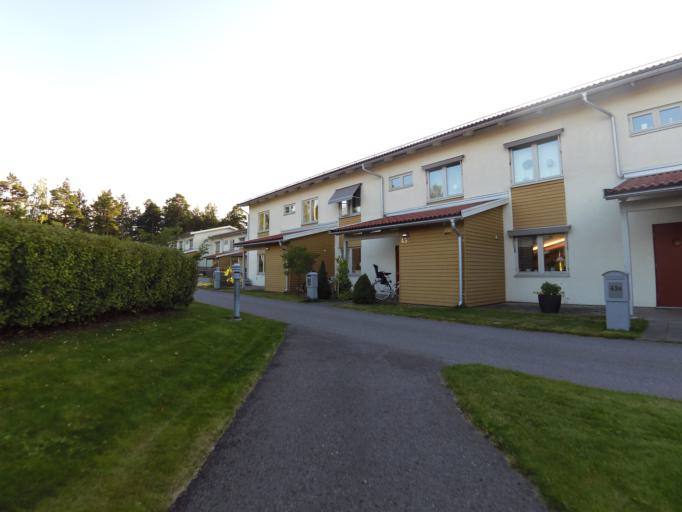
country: SE
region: Gaevleborg
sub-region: Gavle Kommun
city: Gavle
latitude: 60.6560
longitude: 17.1328
